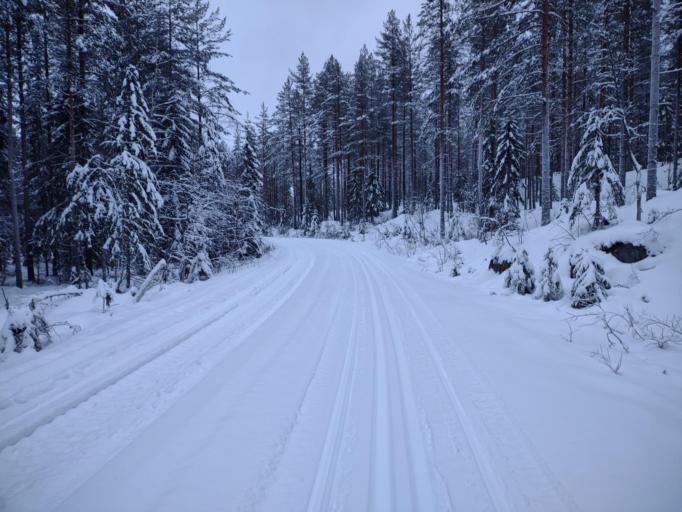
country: NO
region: Buskerud
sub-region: Flesberg
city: Lampeland
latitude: 59.7227
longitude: 9.5425
